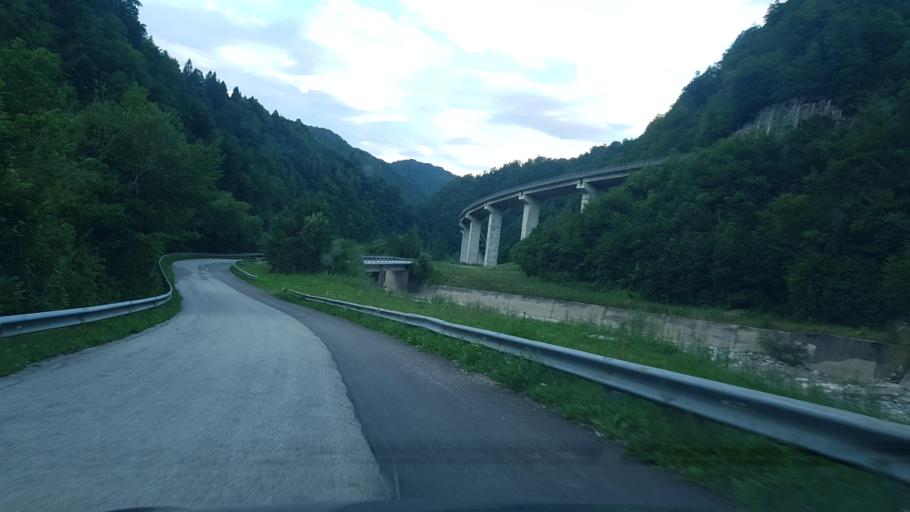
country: IT
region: Friuli Venezia Giulia
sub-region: Provincia di Udine
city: Paularo
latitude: 46.4853
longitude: 13.0951
